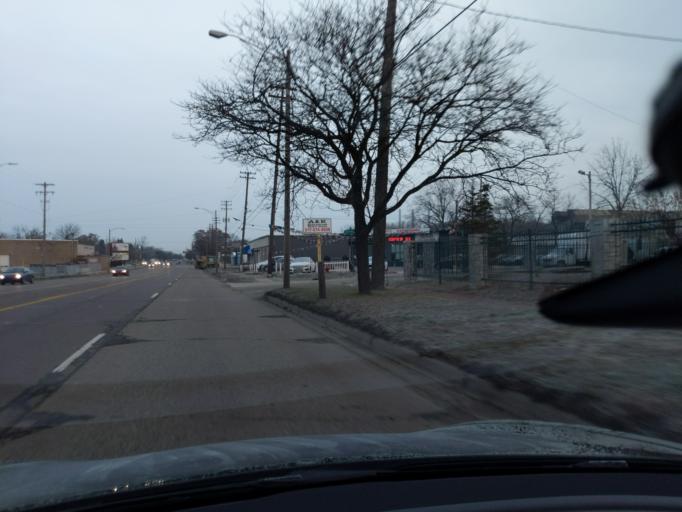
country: US
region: Michigan
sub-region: Ingham County
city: Lansing
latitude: 42.7022
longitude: -84.5673
